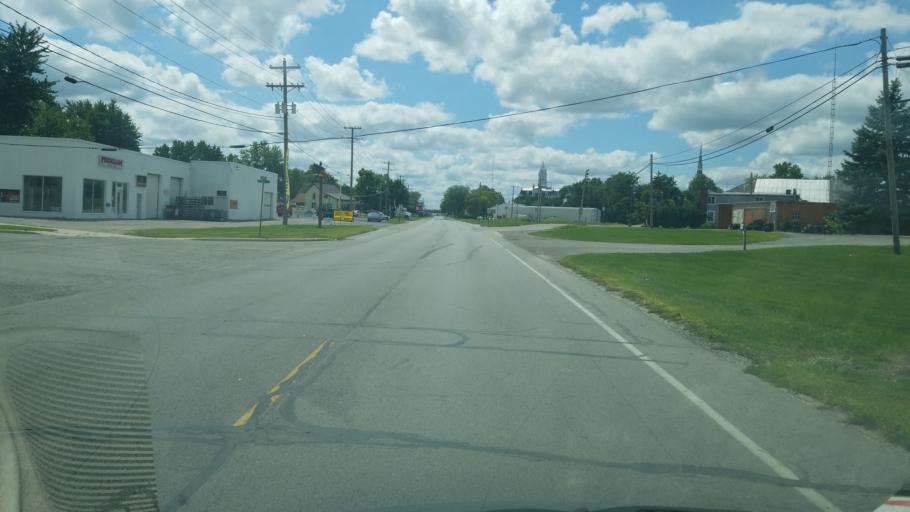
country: US
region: Ohio
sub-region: Henry County
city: Napoleon
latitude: 41.3951
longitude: -84.1186
